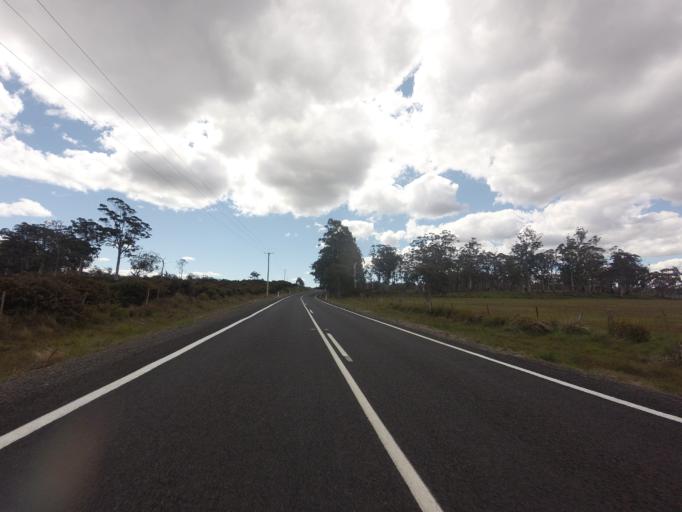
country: AU
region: Tasmania
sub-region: Northern Midlands
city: Evandale
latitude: -41.9832
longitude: 147.6669
